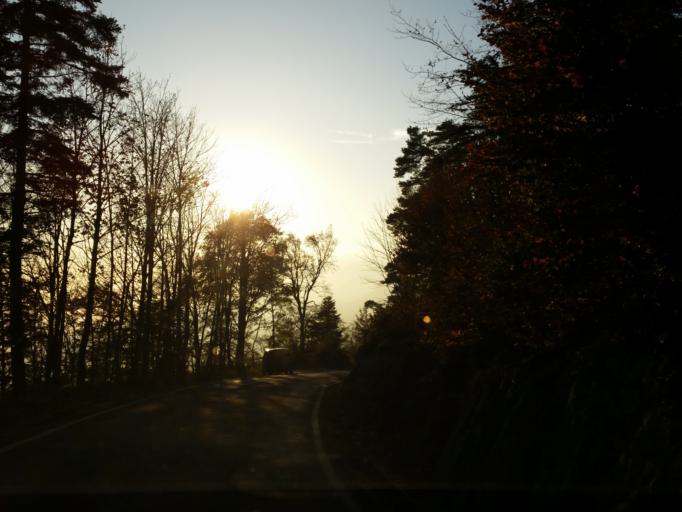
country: CH
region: Solothurn
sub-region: Bezirk Lebern
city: Langendorf
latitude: 47.2416
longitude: 7.4979
